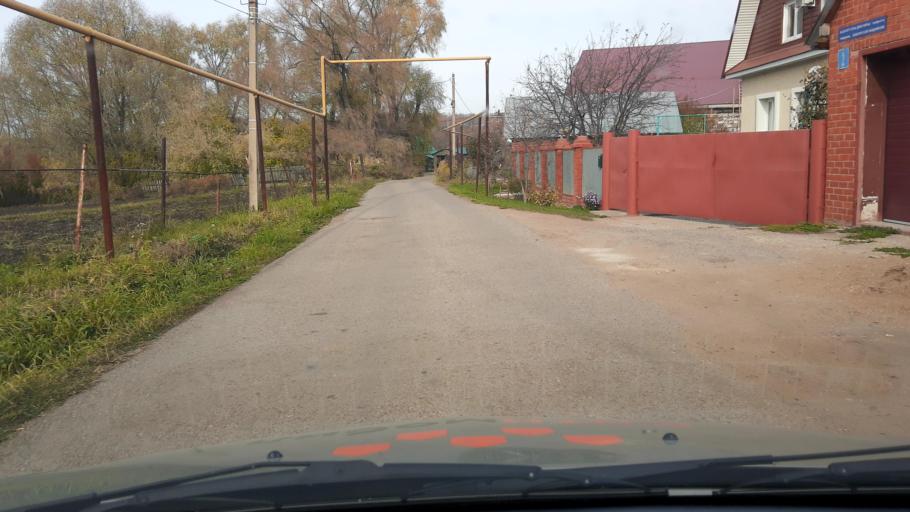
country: RU
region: Bashkortostan
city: Avdon
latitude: 54.7028
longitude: 55.7993
